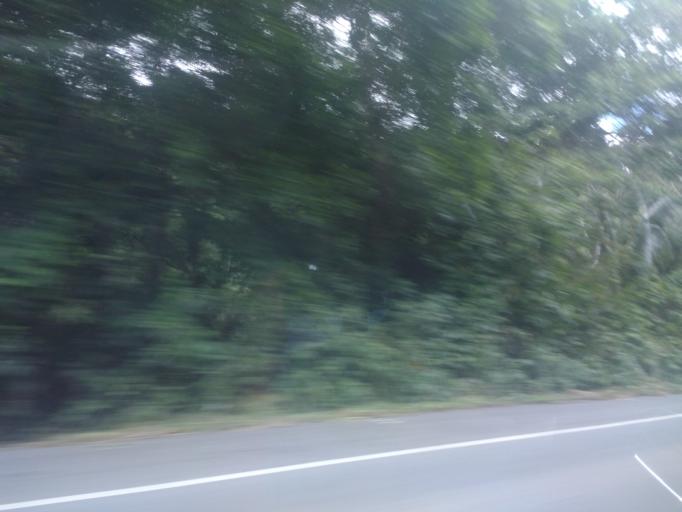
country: BR
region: Alagoas
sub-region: Messias
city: Messias
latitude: -9.3555
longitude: -35.8539
